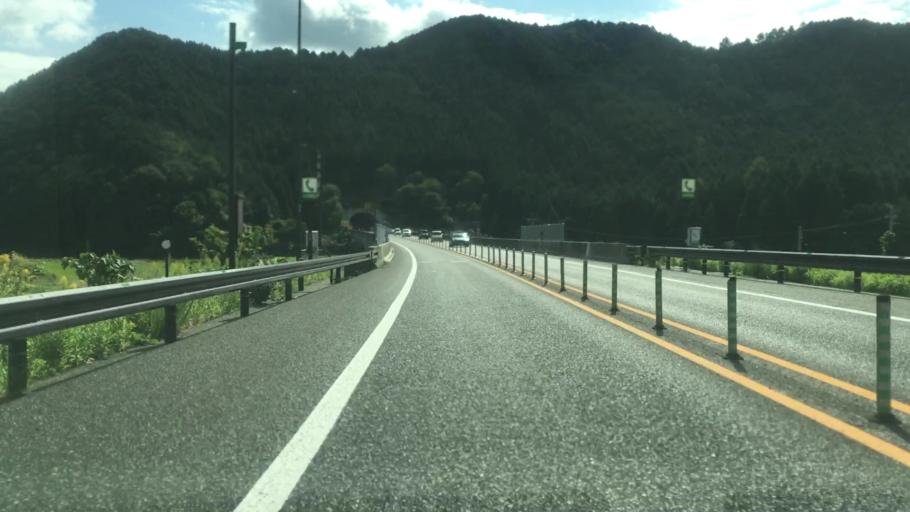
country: JP
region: Kyoto
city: Fukuchiyama
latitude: 35.2308
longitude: 135.0232
